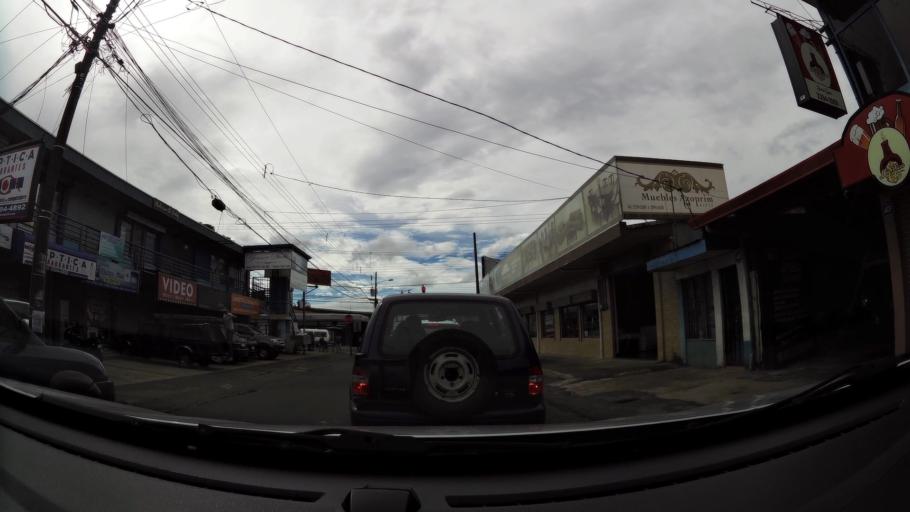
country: CR
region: San Jose
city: Ipis
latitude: 9.9763
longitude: -84.0099
